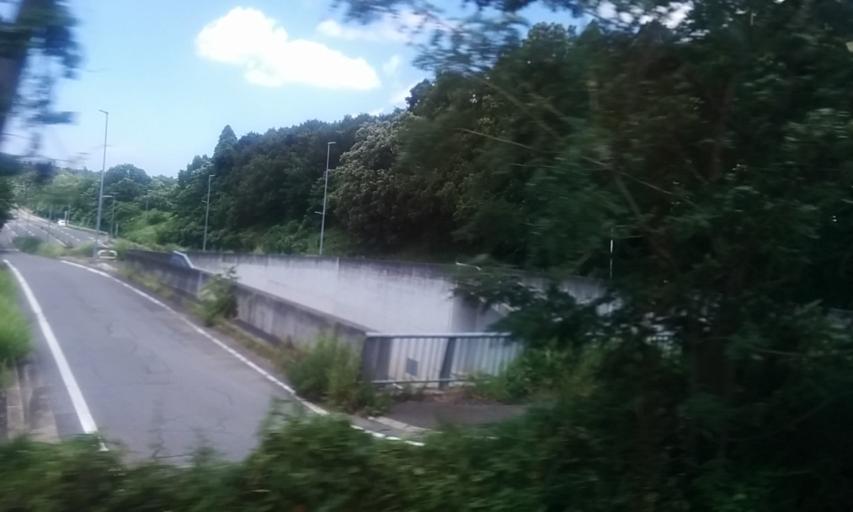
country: JP
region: Chiba
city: Chiba
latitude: 35.5644
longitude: 140.1687
